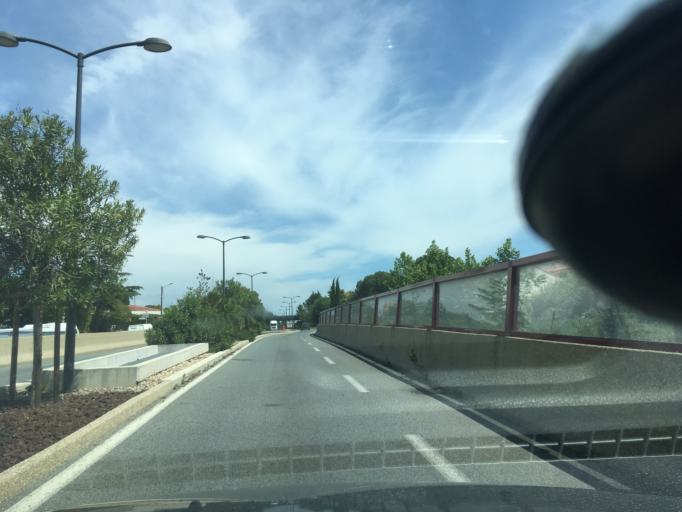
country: FR
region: Provence-Alpes-Cote d'Azur
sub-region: Departement du Var
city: Puget-sur-Argens
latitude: 43.4577
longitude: 6.6836
